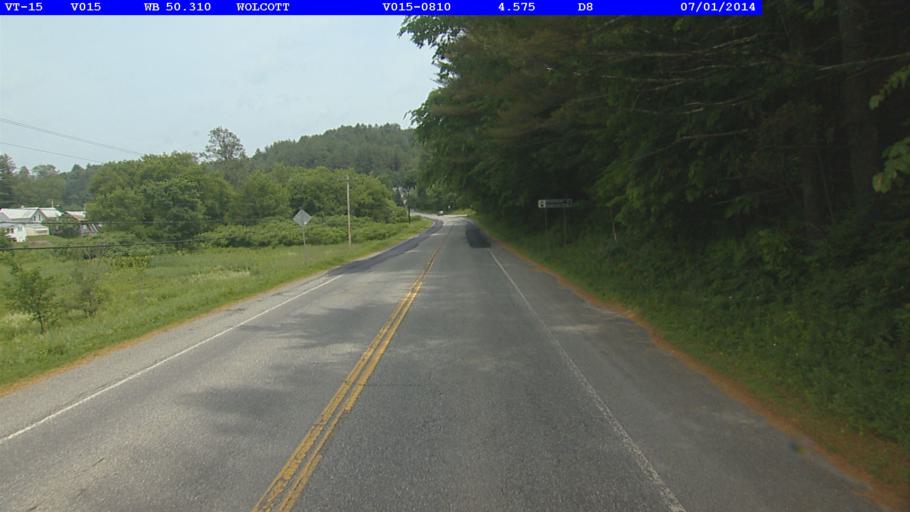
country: US
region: Vermont
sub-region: Caledonia County
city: Hardwick
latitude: 44.5431
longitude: -72.4561
